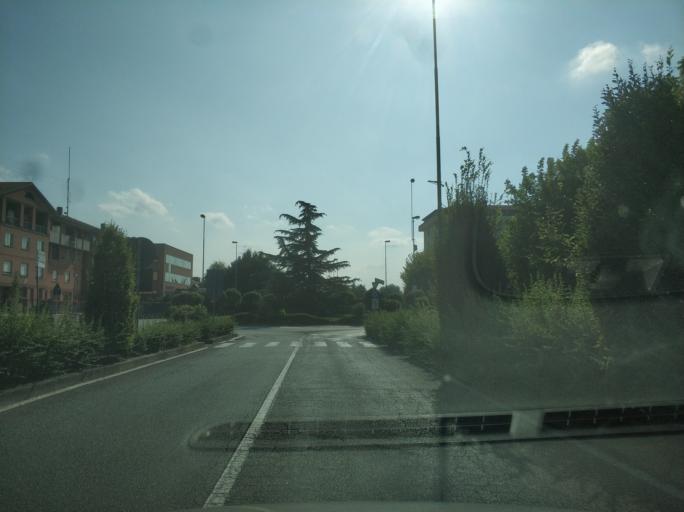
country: IT
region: Piedmont
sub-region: Provincia di Cuneo
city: Bra
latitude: 44.7007
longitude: 7.8389
